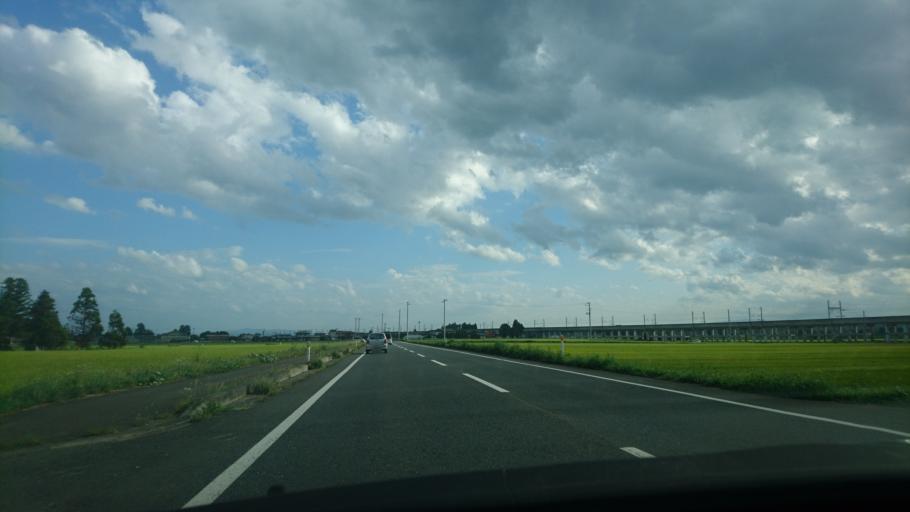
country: JP
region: Iwate
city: Kitakami
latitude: 39.2437
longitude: 141.1180
